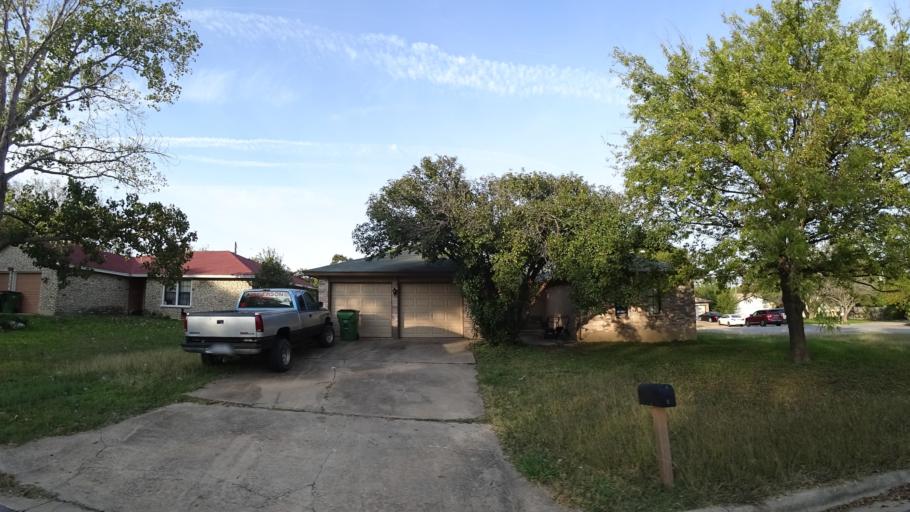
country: US
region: Texas
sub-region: Williamson County
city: Round Rock
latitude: 30.4976
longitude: -97.6665
